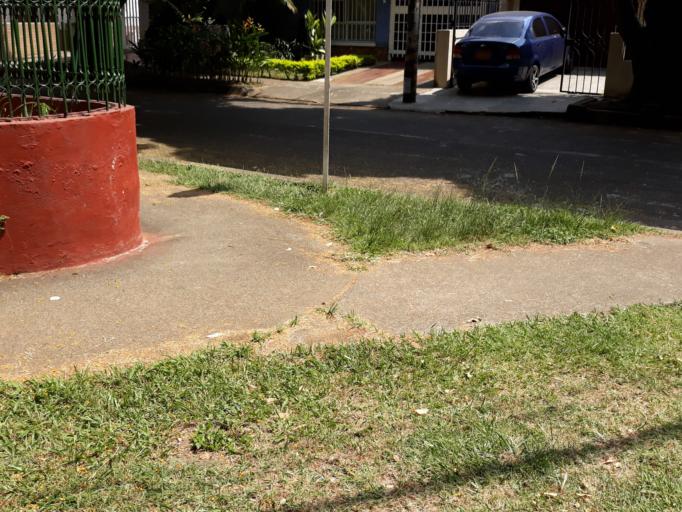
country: CO
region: Valle del Cauca
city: Cali
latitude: 3.3823
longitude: -76.5400
